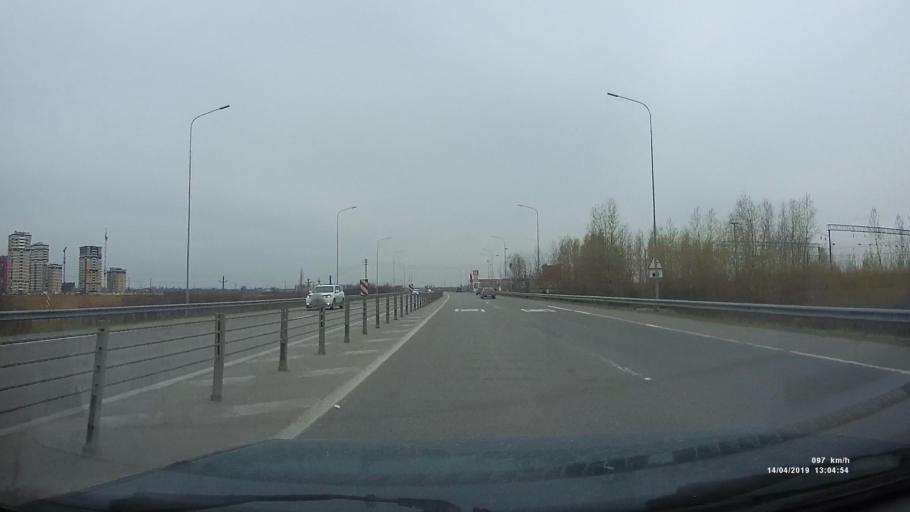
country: RU
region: Rostov
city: Bataysk
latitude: 47.1546
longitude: 39.7210
